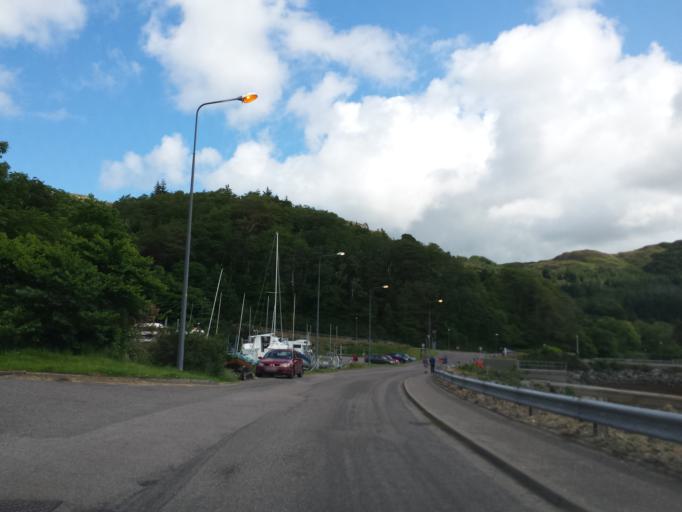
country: GB
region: Scotland
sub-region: Highland
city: Ullapool
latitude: 57.7122
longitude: -5.6805
